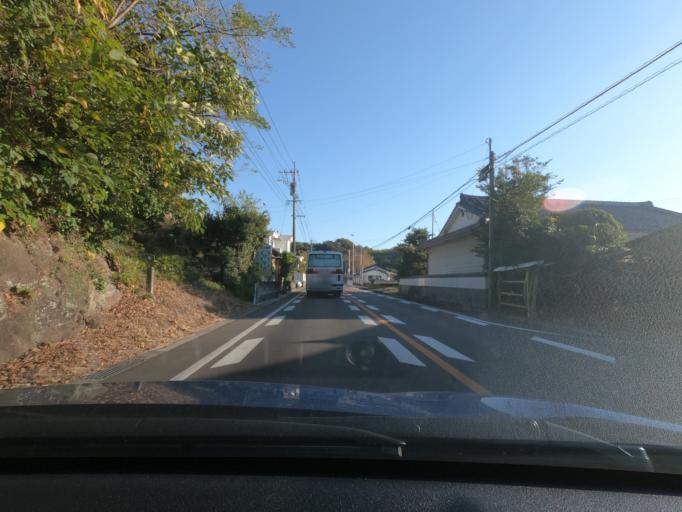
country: JP
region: Kagoshima
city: Akune
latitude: 31.9913
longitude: 130.1978
